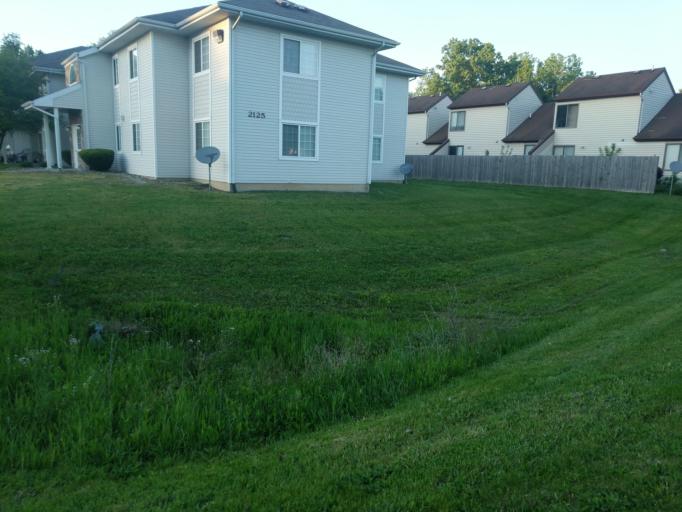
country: US
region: Michigan
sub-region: Ingham County
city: Lansing
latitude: 42.6965
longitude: -84.5203
